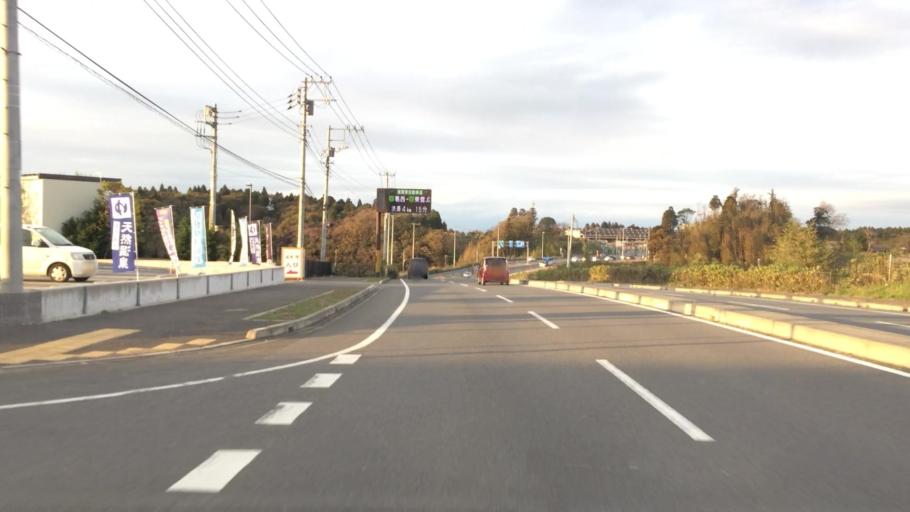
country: JP
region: Chiba
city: Shisui
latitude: 35.7195
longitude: 140.2946
